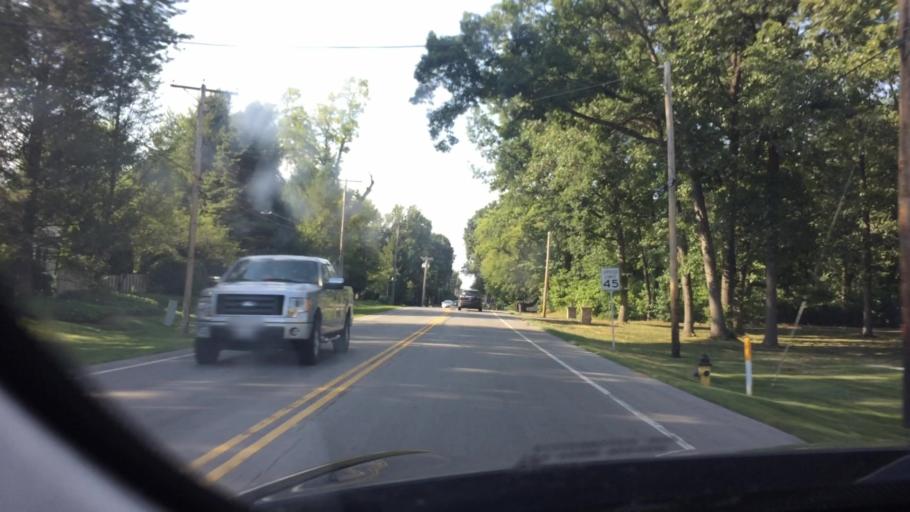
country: US
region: Ohio
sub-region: Lucas County
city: Holland
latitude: 41.6630
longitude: -83.7223
